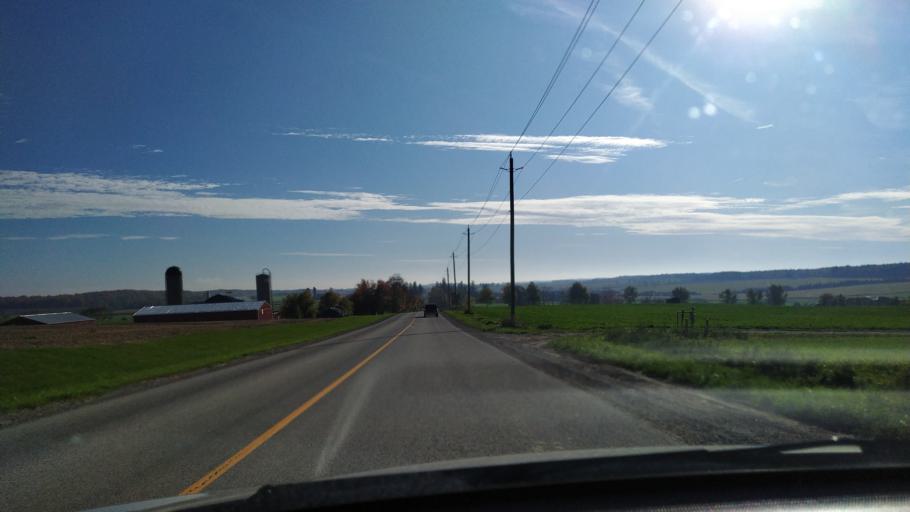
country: CA
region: Ontario
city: Waterloo
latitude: 43.4944
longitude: -80.7459
